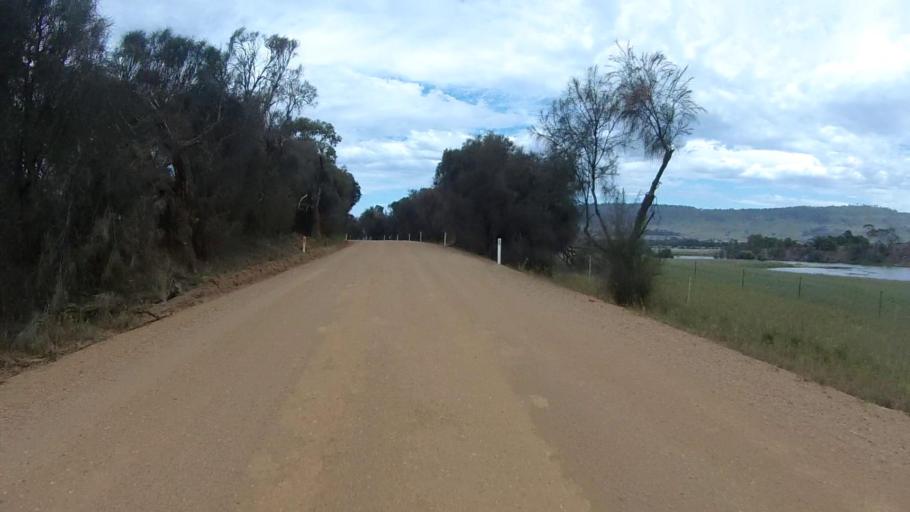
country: AU
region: Tasmania
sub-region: Sorell
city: Sorell
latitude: -42.6997
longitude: 147.4594
